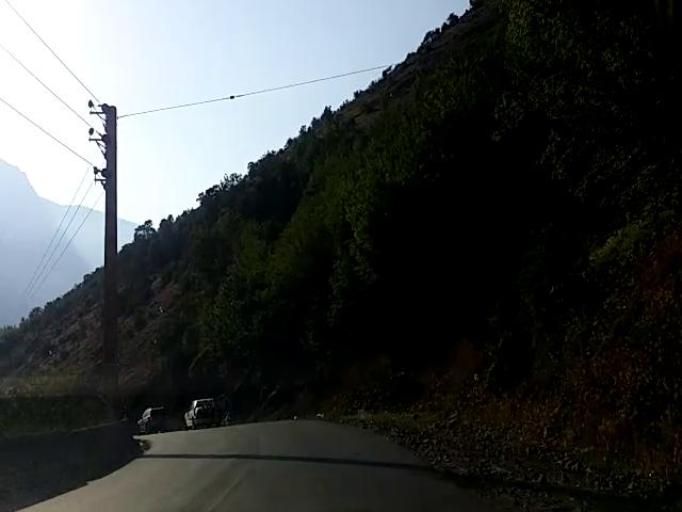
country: IR
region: Mazandaran
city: Chalus
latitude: 36.2691
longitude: 51.2605
